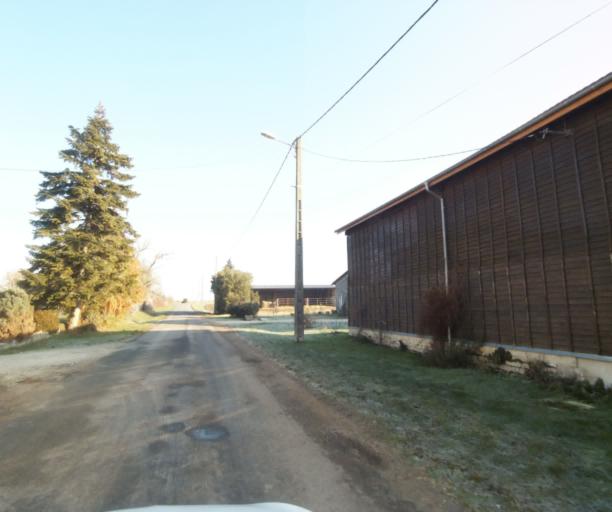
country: FR
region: Champagne-Ardenne
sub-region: Departement de la Haute-Marne
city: Montier-en-Der
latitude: 48.5037
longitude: 4.7280
